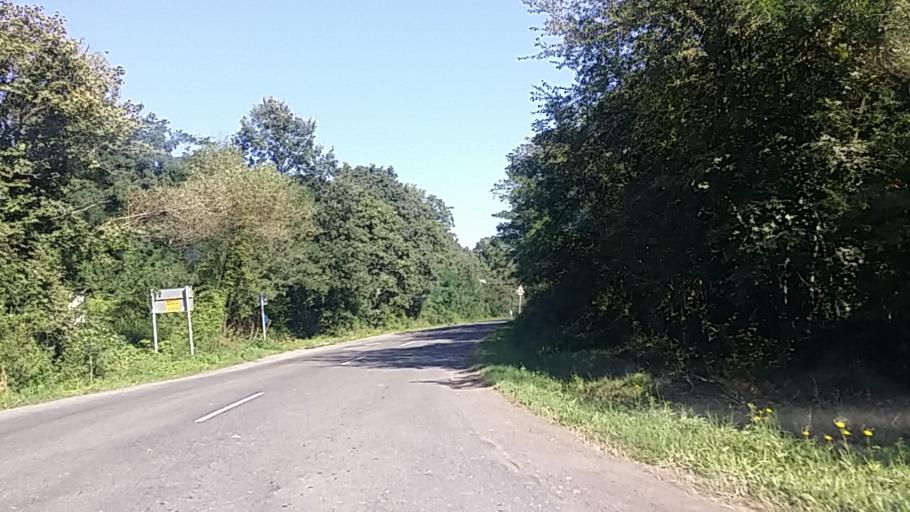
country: HU
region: Nograd
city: Bujak
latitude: 47.9334
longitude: 19.6099
